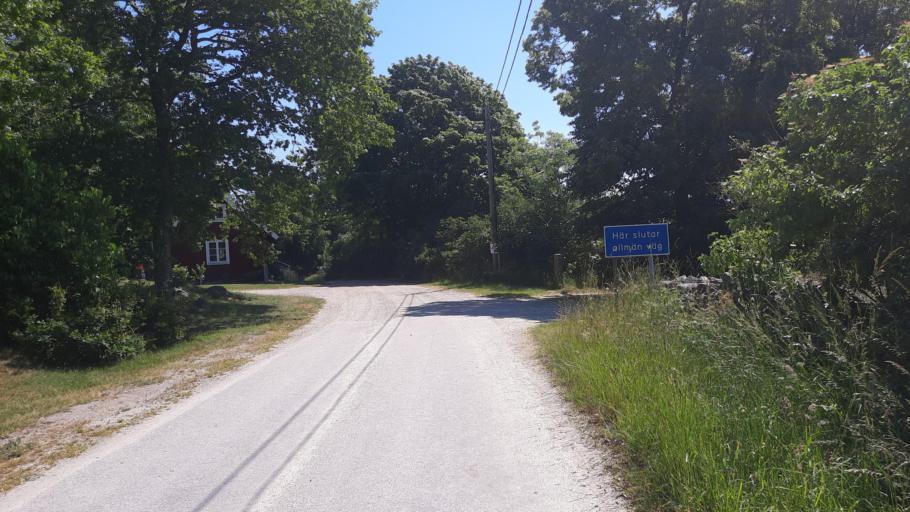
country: SE
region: Blekinge
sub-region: Karlskrona Kommun
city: Jaemjoe
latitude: 56.1465
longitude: 15.7726
